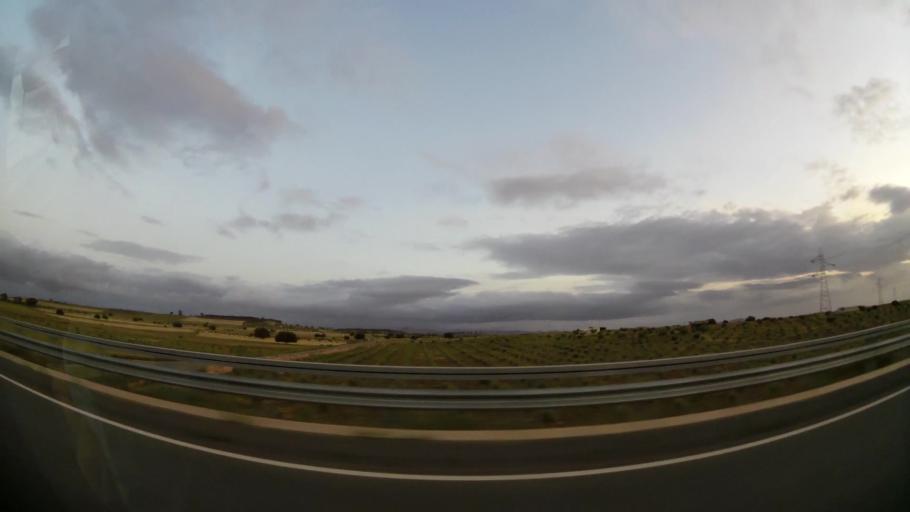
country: MA
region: Oriental
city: El Aioun
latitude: 34.6248
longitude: -2.5047
